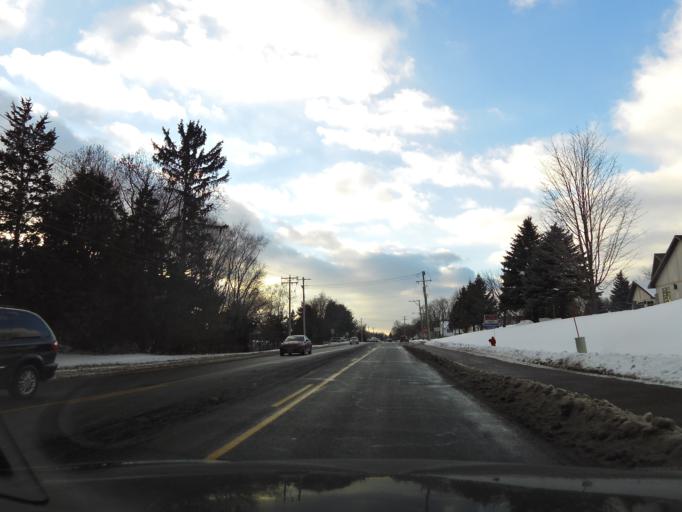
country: US
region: Wisconsin
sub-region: Saint Croix County
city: Hudson
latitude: 44.9779
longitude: -92.7288
